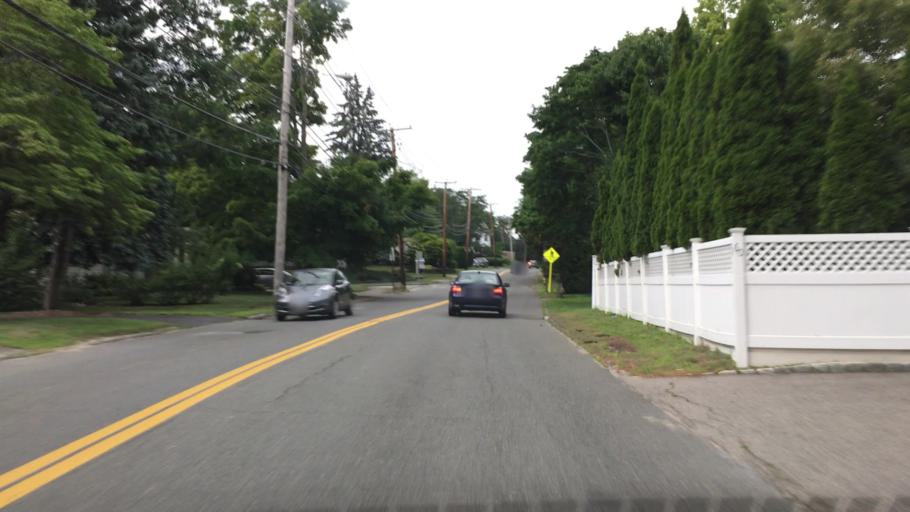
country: US
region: Massachusetts
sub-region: Middlesex County
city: Waltham
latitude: 42.4125
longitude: -71.2538
